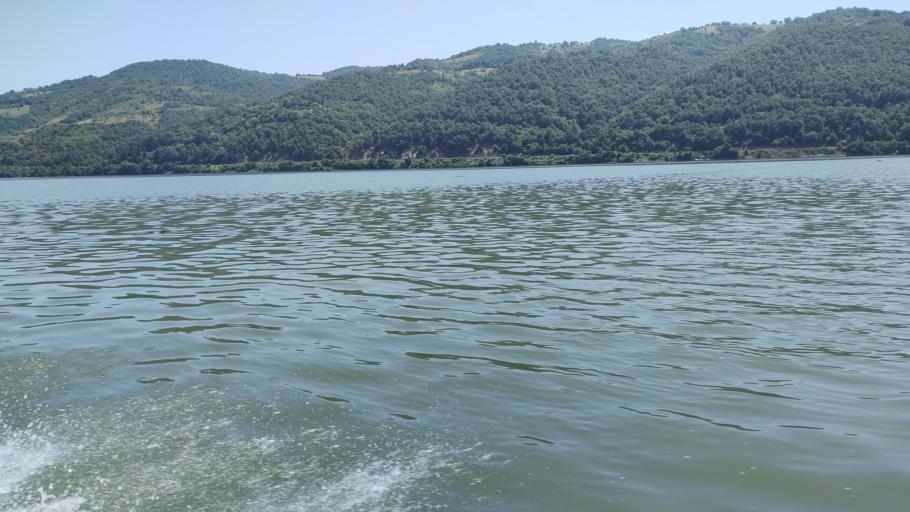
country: RO
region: Mehedinti
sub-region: Comuna Svinita
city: Svinita
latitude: 44.5115
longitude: 22.1963
